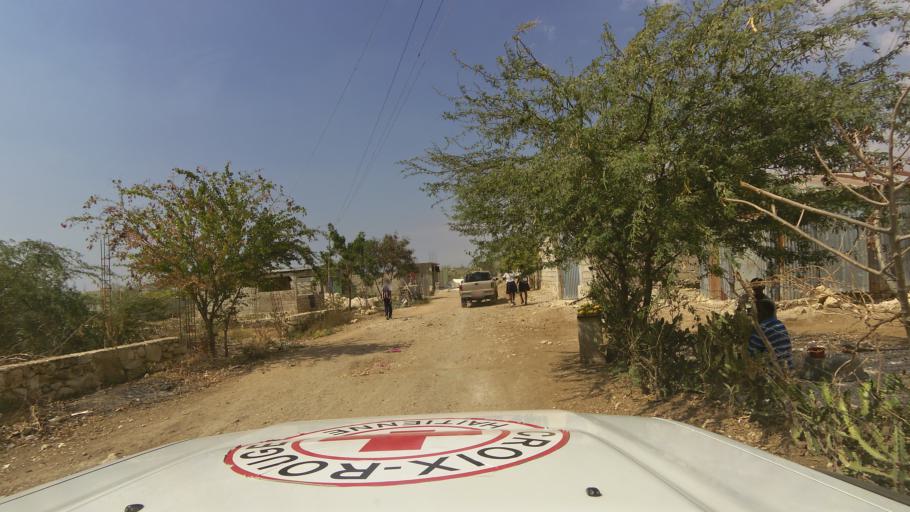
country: HT
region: Ouest
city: Croix des Bouquets
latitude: 18.6490
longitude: -72.2647
